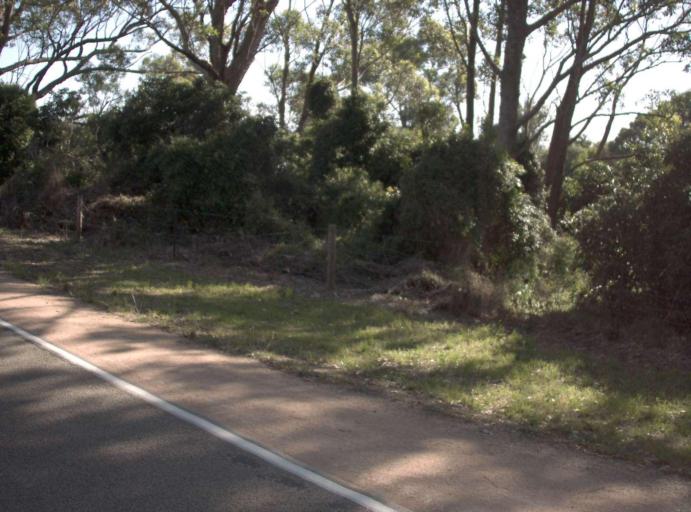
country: AU
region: Victoria
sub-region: East Gippsland
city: Lakes Entrance
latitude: -37.7368
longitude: 148.5047
